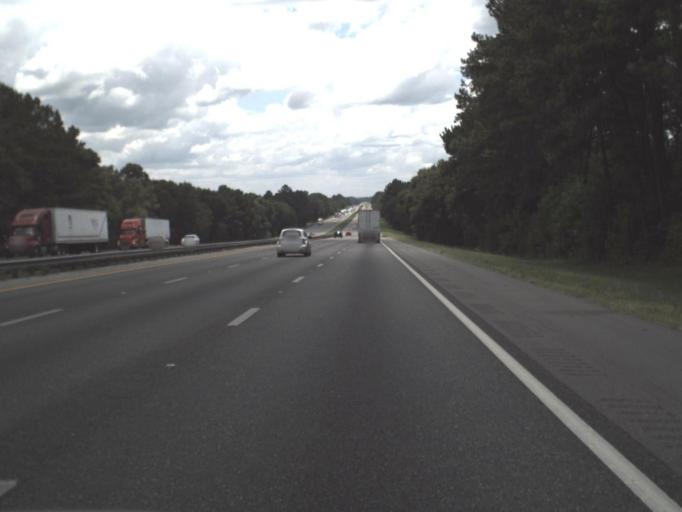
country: US
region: Florida
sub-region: Alachua County
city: High Springs
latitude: 29.9366
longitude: -82.5633
